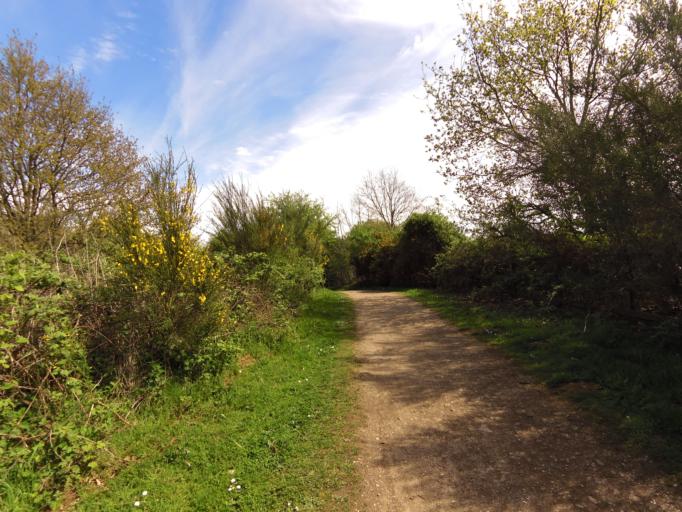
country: GB
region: England
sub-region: Essex
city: Mistley
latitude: 51.9856
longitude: 1.1092
